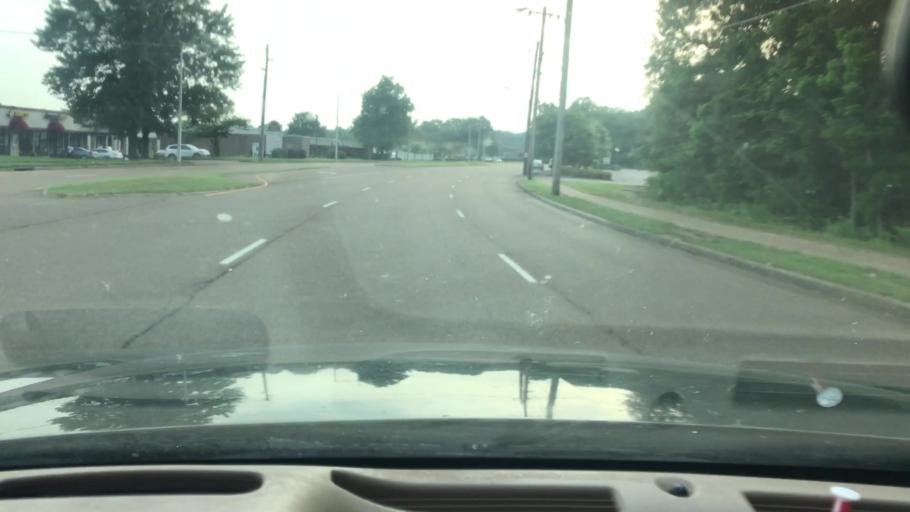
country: US
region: Tennessee
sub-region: Shelby County
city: Bartlett
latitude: 35.1999
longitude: -89.8680
